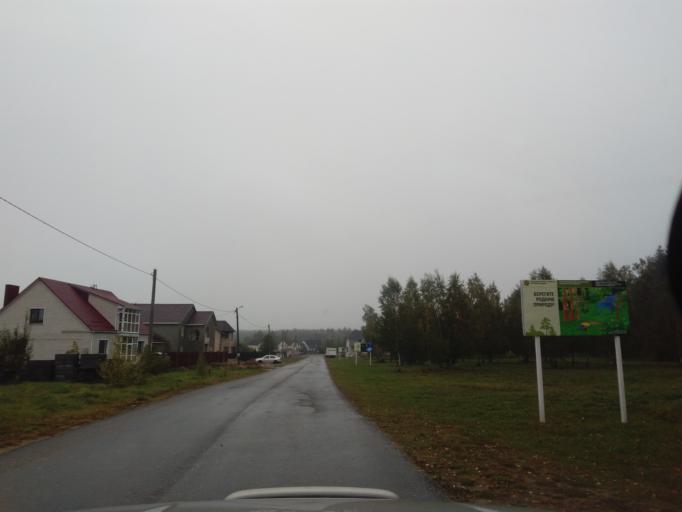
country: BY
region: Minsk
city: Kapyl'
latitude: 53.1559
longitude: 27.0976
